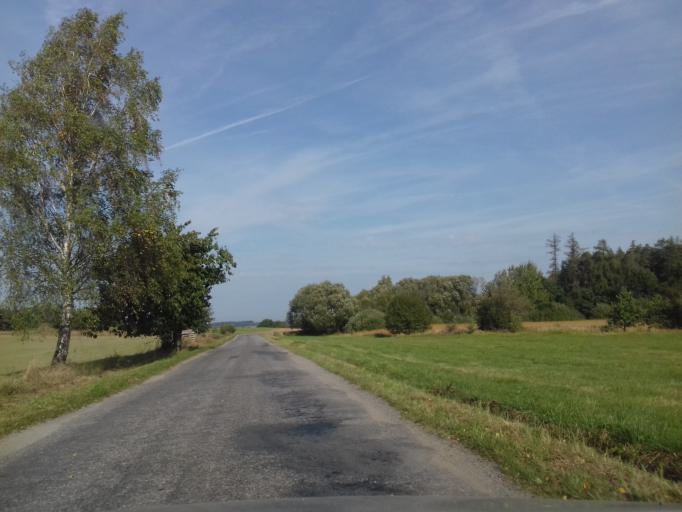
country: CZ
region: Central Bohemia
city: Kosova Hora
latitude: 49.6622
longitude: 14.5385
